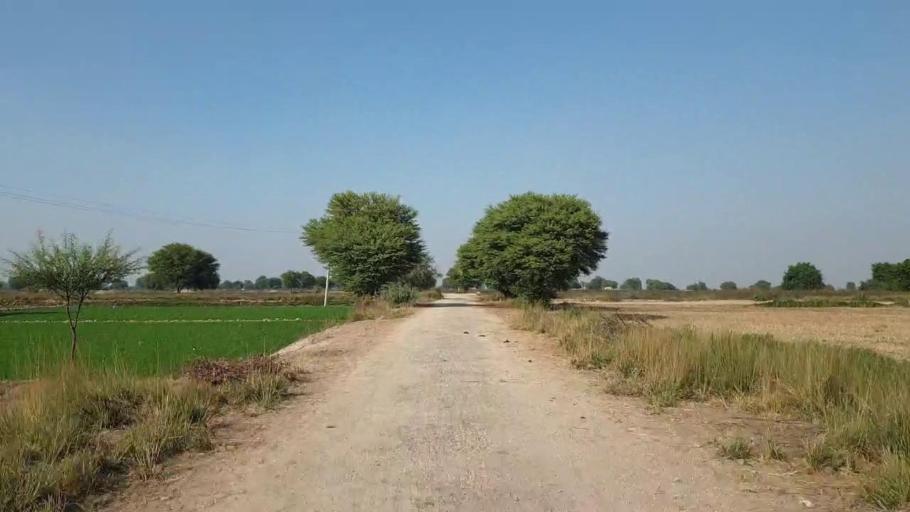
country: PK
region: Sindh
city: Sehwan
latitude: 26.4565
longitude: 67.8158
